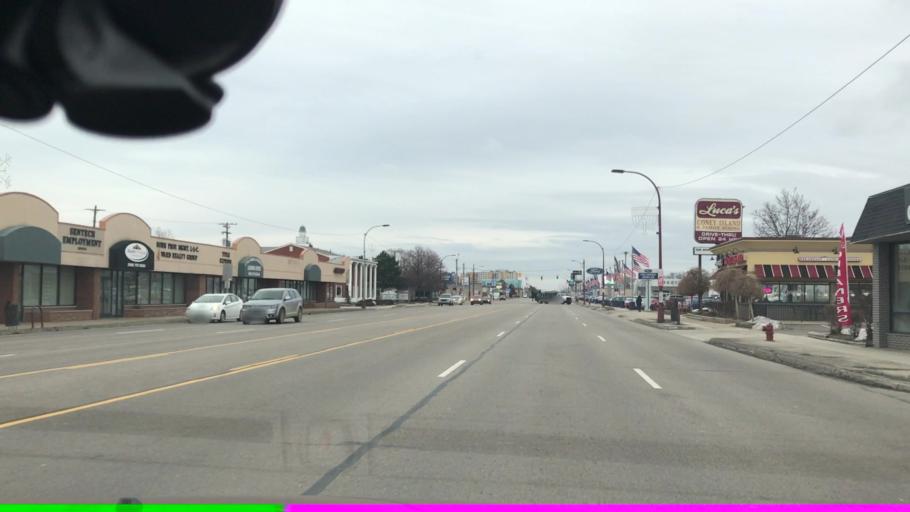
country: US
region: Michigan
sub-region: Macomb County
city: Center Line
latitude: 42.4899
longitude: -83.0278
